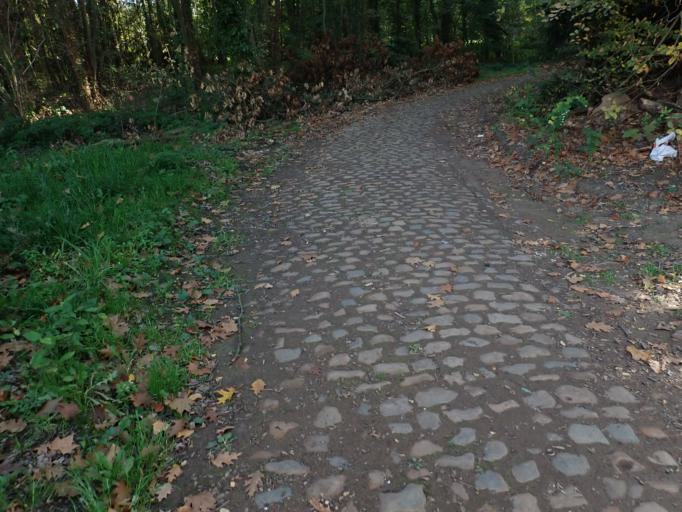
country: BE
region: Flanders
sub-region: Provincie Vlaams-Brabant
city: Holsbeek
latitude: 50.9434
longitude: 4.7611
